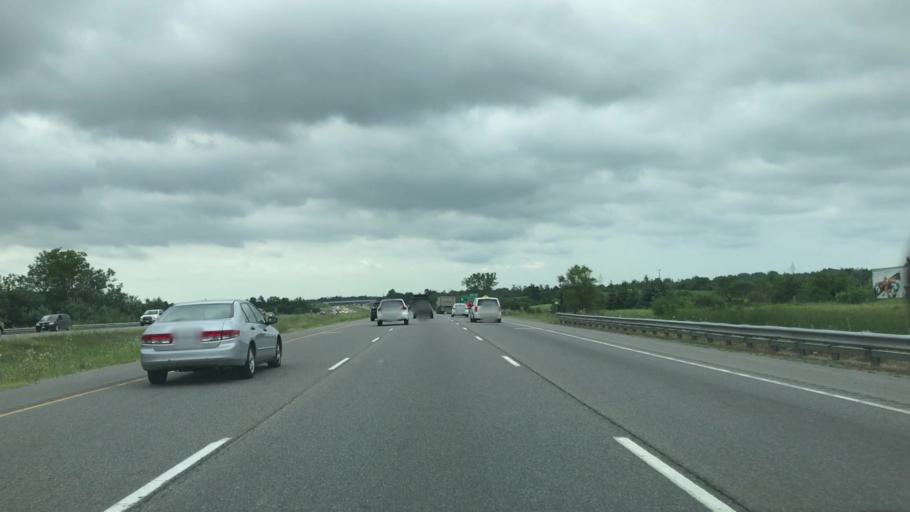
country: CA
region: Ontario
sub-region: York
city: Richmond Hill
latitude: 43.9541
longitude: -79.3930
